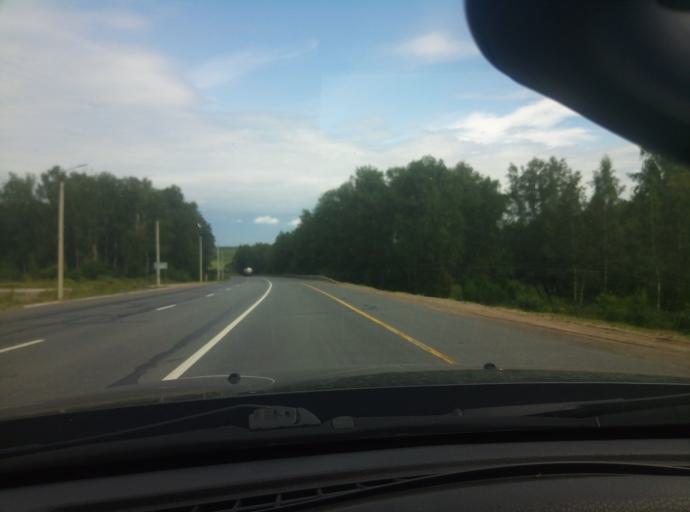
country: RU
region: Tula
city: Barsuki
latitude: 54.2876
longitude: 37.5380
